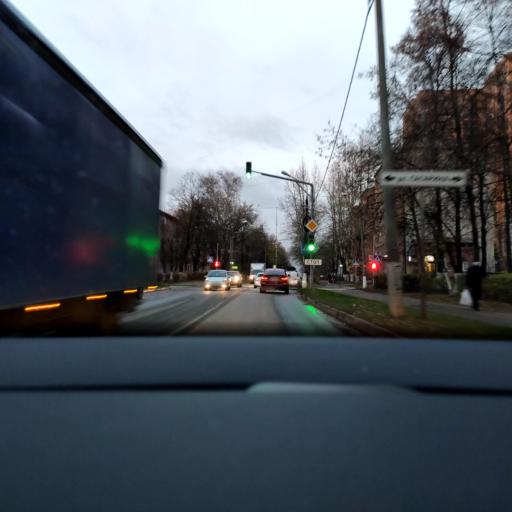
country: RU
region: Moskovskaya
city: Reutov
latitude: 55.7639
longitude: 37.8633
